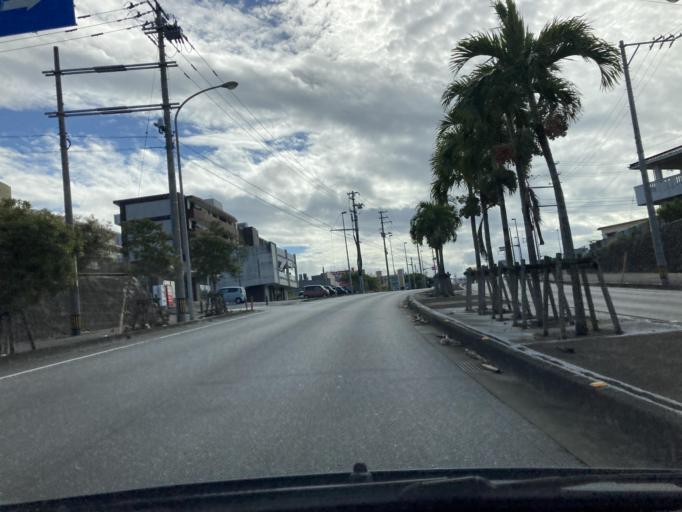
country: JP
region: Okinawa
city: Tomigusuku
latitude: 26.1648
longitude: 127.7251
